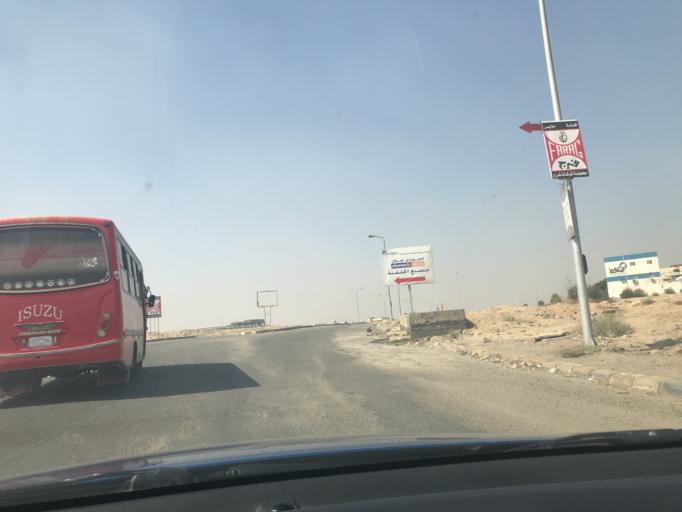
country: EG
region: Eastern Province
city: Bilbays
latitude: 30.2530
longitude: 31.7574
